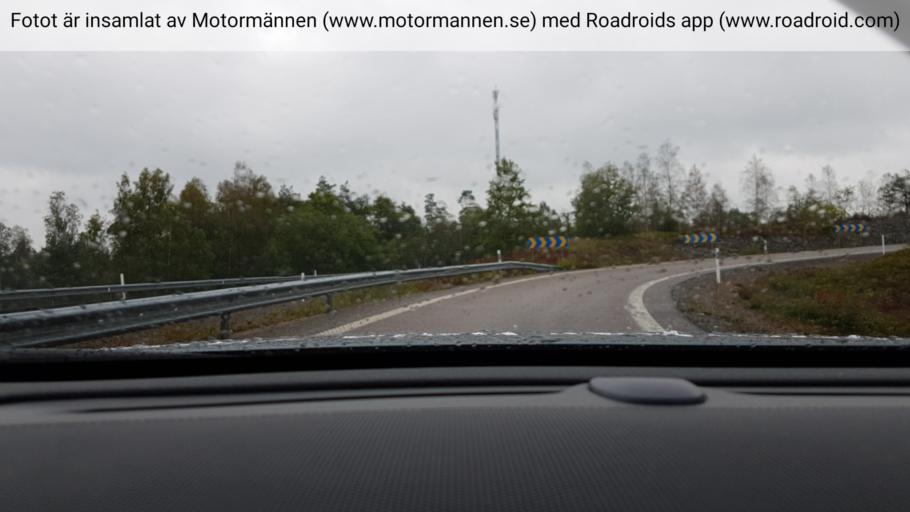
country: SE
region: Vaestra Goetaland
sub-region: Vanersborgs Kommun
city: Vanersborg
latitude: 58.3908
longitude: 12.2892
